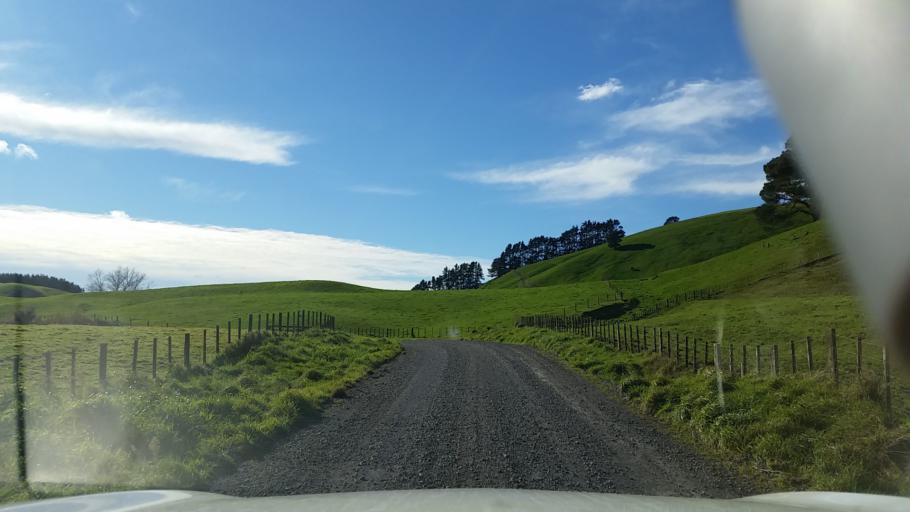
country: NZ
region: Bay of Plenty
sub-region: Rotorua District
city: Rotorua
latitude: -38.3575
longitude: 176.2315
